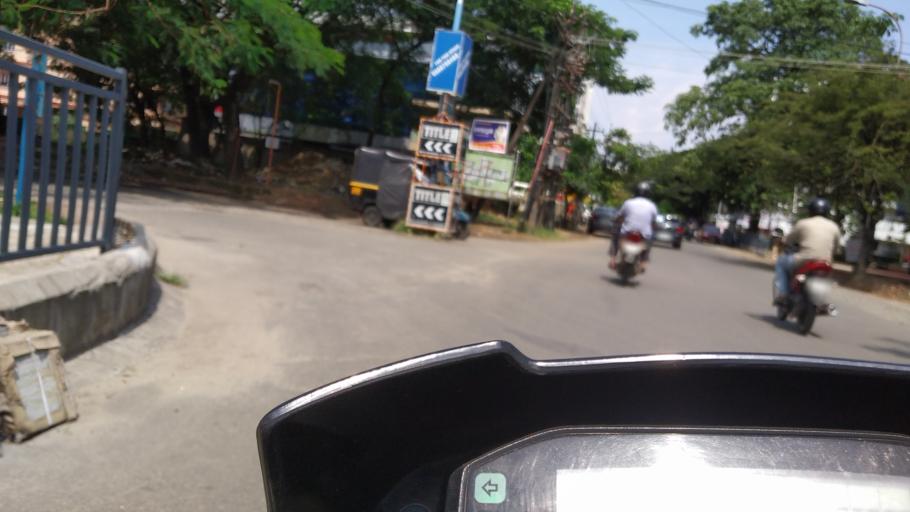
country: IN
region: Kerala
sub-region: Ernakulam
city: Cochin
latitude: 9.9717
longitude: 76.3014
